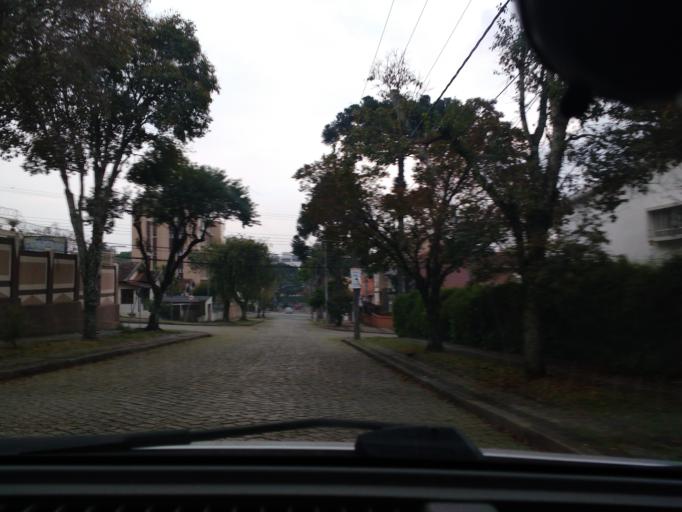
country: BR
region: Parana
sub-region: Curitiba
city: Curitiba
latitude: -25.4241
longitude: -49.2786
